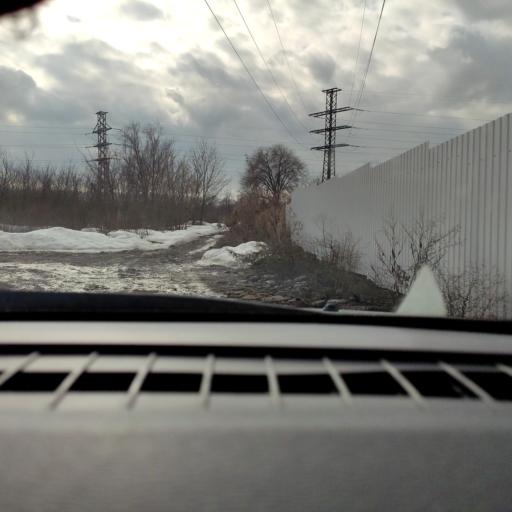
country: RU
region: Samara
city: Petra-Dubrava
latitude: 53.2886
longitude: 50.3107
